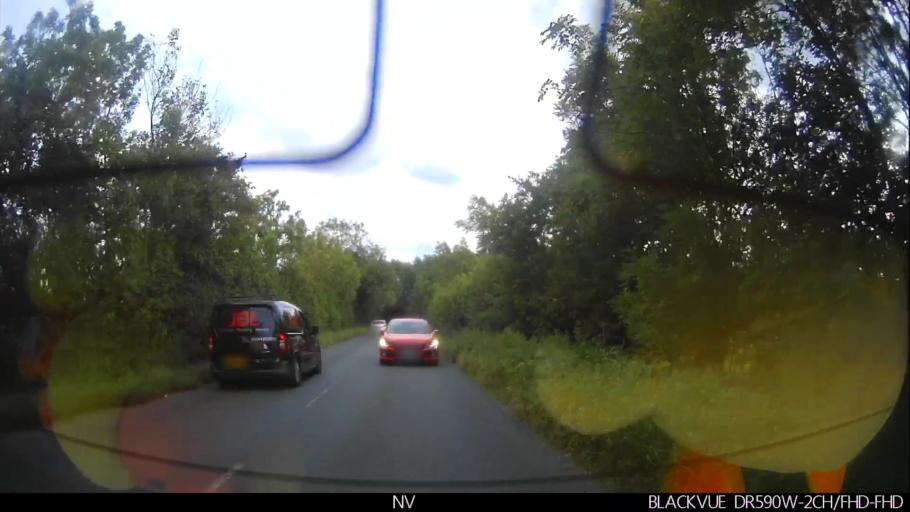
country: GB
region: England
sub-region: City of York
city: Holtby
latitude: 54.0472
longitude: -0.9592
